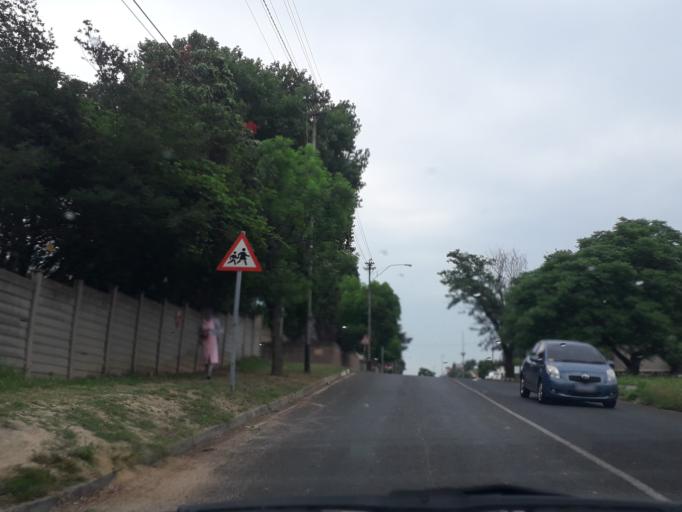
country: ZA
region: Gauteng
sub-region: City of Johannesburg Metropolitan Municipality
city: Johannesburg
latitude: -26.1447
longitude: 28.0974
